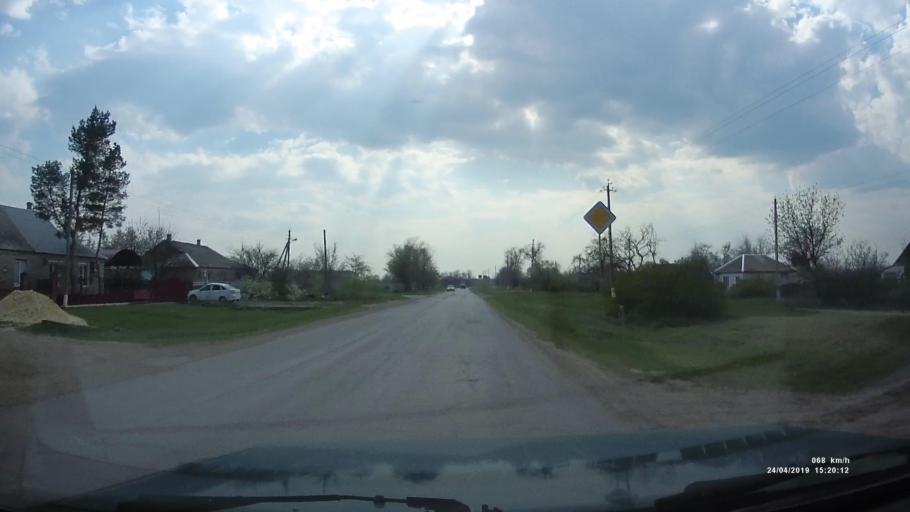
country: RU
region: Rostov
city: Remontnoye
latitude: 46.5363
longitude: 43.1356
